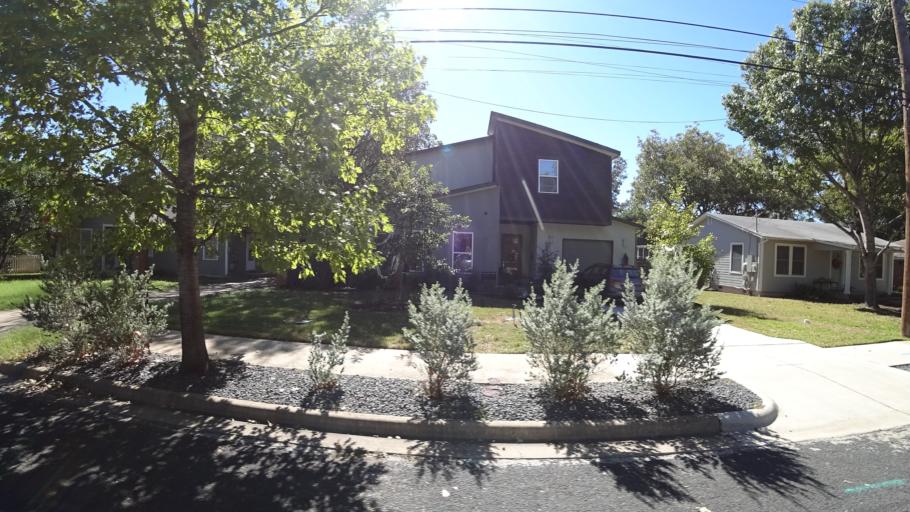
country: US
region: Texas
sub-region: Travis County
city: Austin
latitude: 30.3330
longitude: -97.7276
